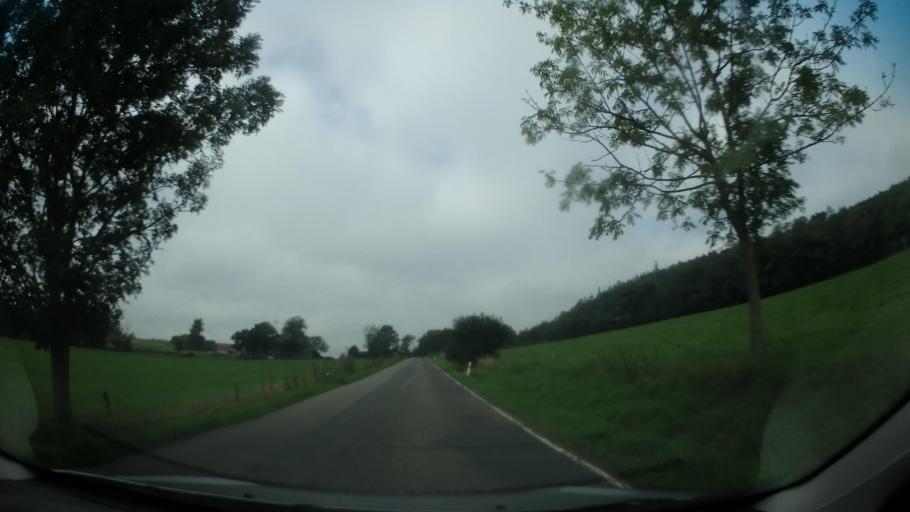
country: CZ
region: Central Bohemia
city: Neveklov
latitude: 49.7360
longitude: 14.4982
